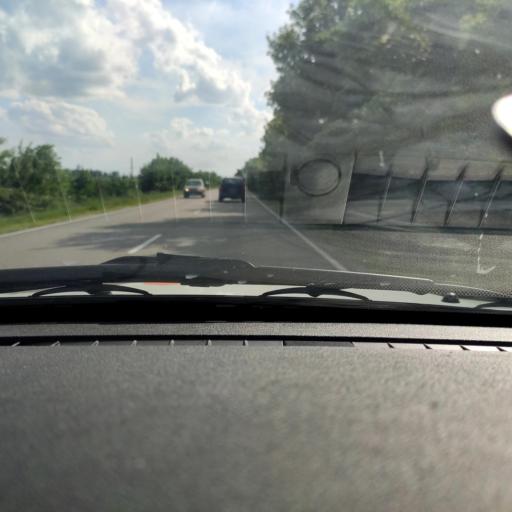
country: RU
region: Voronezj
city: Volya
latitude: 51.6956
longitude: 39.5054
